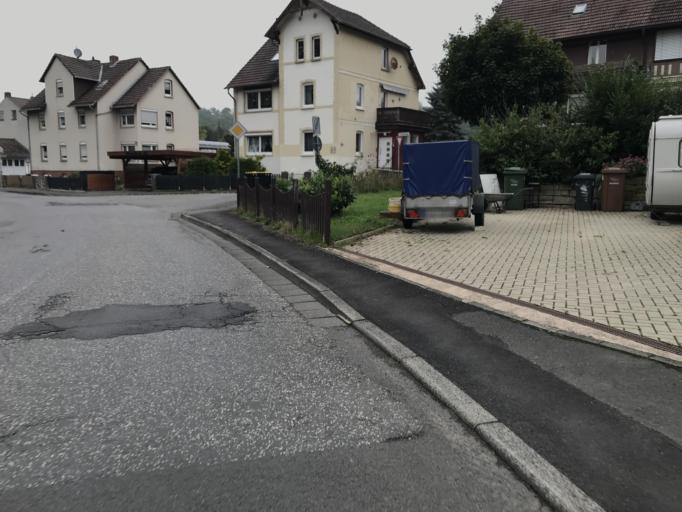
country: DE
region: Hesse
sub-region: Regierungsbezirk Kassel
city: Guxhagen
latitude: 51.2326
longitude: 9.4682
